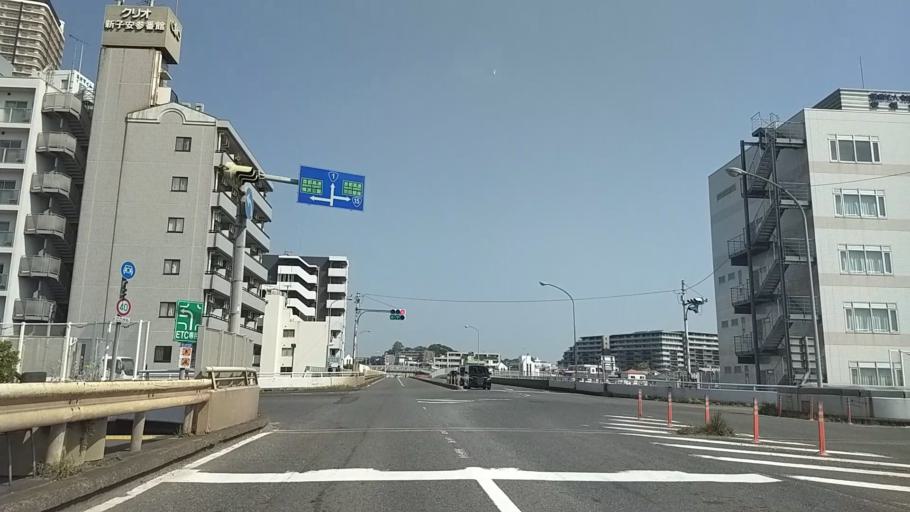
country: JP
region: Kanagawa
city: Yokohama
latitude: 35.4853
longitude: 139.6553
